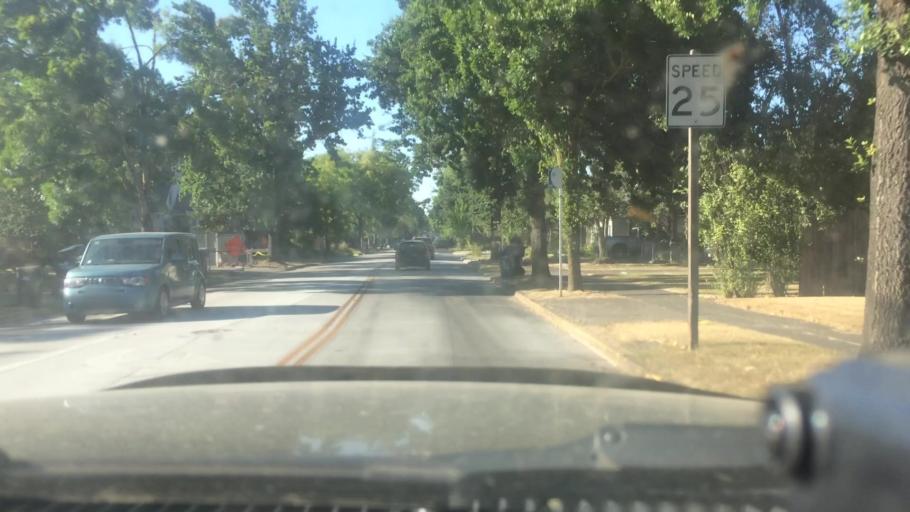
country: US
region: Oregon
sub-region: Lane County
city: Eugene
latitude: 44.0404
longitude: -123.1012
